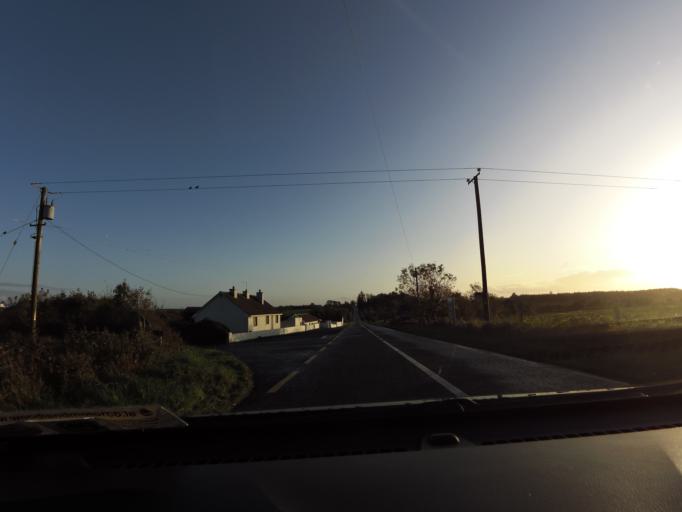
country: IE
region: Connaught
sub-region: Roscommon
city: Castlerea
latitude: 53.7299
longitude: -8.5546
